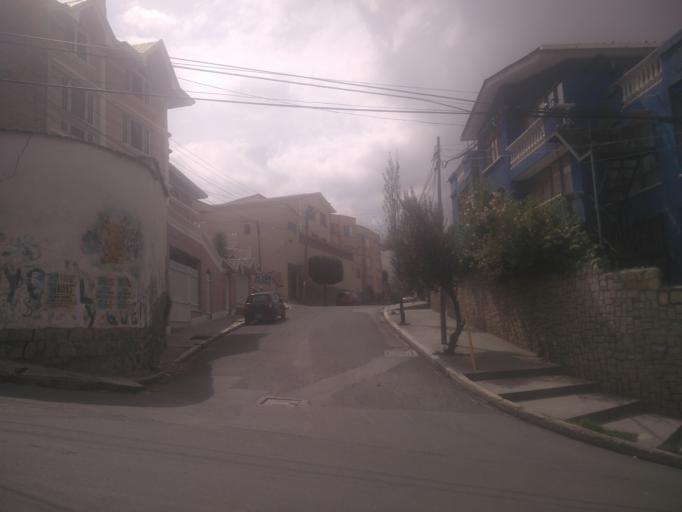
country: BO
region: La Paz
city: La Paz
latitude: -16.5131
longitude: -68.1316
